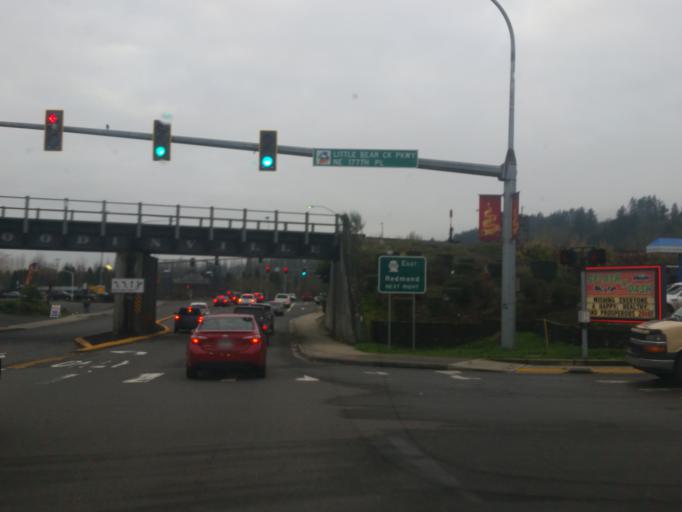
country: US
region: Washington
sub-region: King County
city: Woodinville
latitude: 47.7556
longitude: -122.1656
